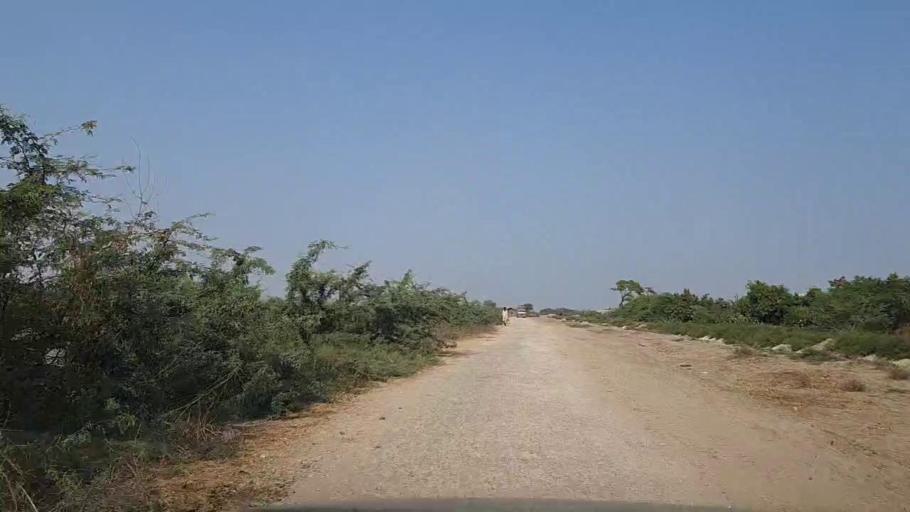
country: PK
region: Sindh
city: Chuhar Jamali
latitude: 24.5222
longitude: 67.9262
